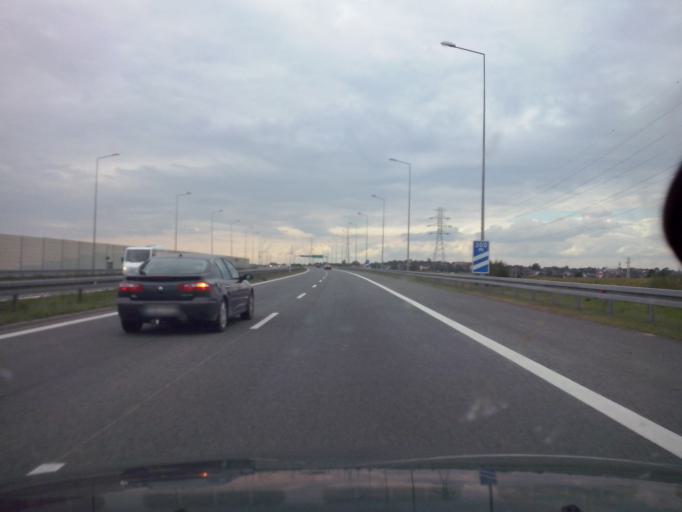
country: PL
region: Lesser Poland Voivodeship
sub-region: Powiat wielicki
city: Targowisko
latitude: 49.9899
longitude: 20.2849
